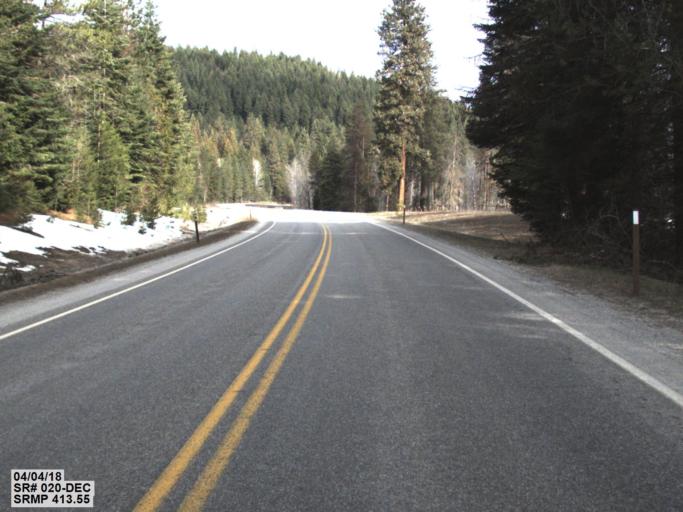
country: US
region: Washington
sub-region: Pend Oreille County
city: Newport
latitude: 48.4149
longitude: -117.3151
